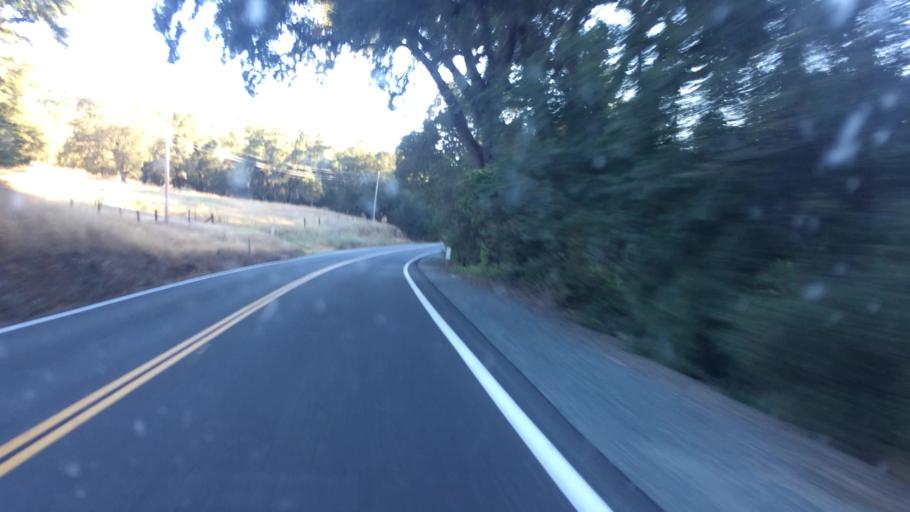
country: US
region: California
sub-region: Amador County
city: Plymouth
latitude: 38.5063
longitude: -120.8485
